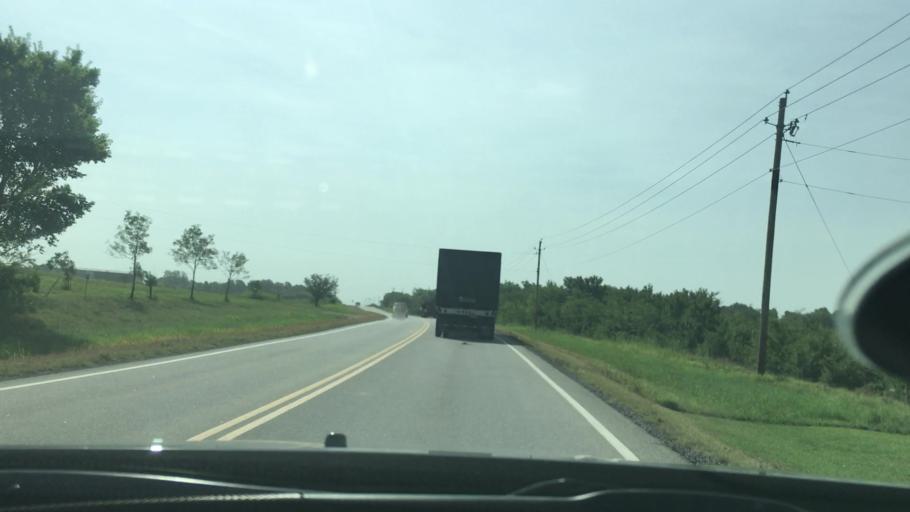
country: US
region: Oklahoma
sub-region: Atoka County
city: Atoka
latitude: 34.3992
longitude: -96.1706
